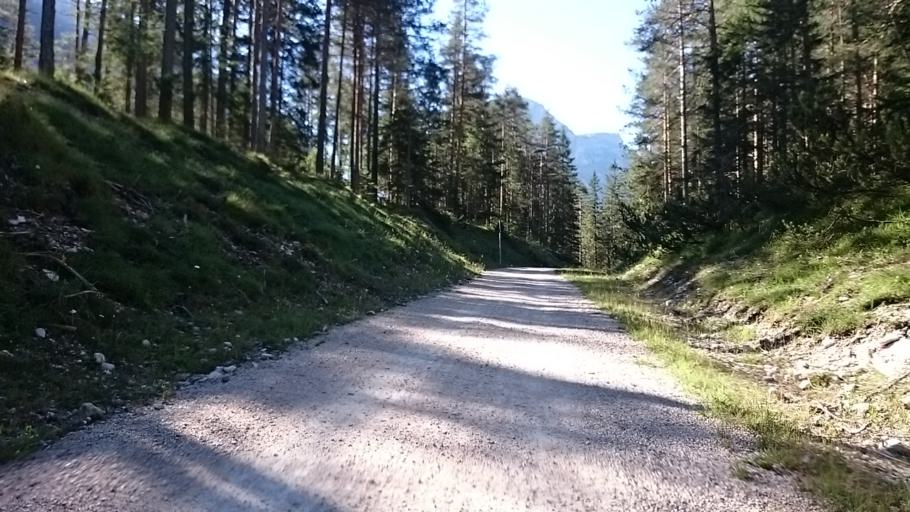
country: IT
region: Trentino-Alto Adige
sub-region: Bolzano
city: Dobbiaco
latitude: 46.6508
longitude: 12.2282
